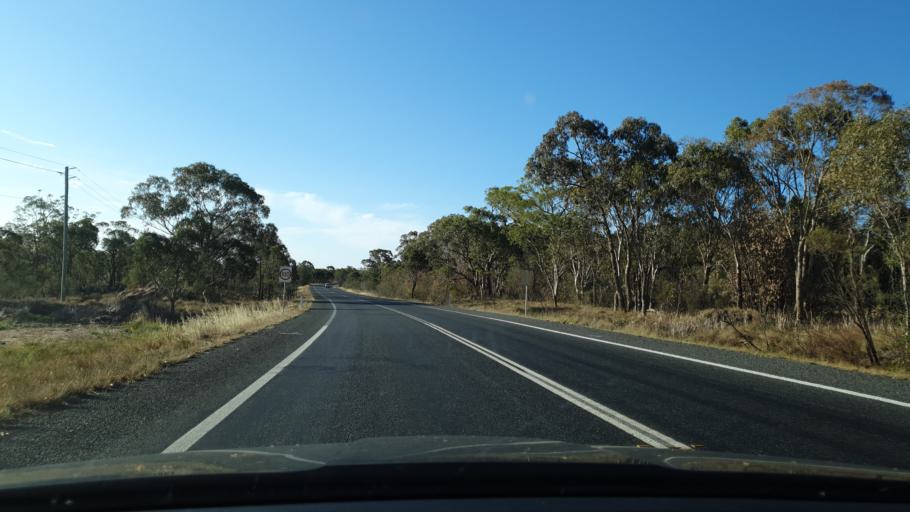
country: AU
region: Queensland
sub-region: Southern Downs
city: Stanthorpe
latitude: -28.6727
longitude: 151.9194
